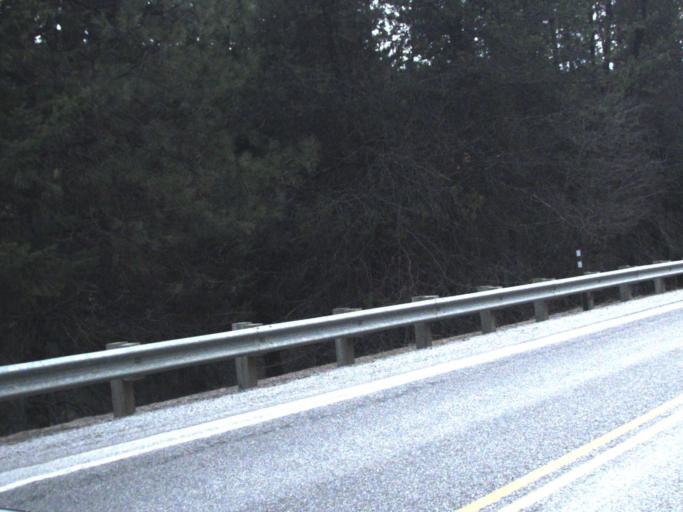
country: US
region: Washington
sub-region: Pend Oreille County
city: Newport
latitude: 48.5408
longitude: -117.3052
